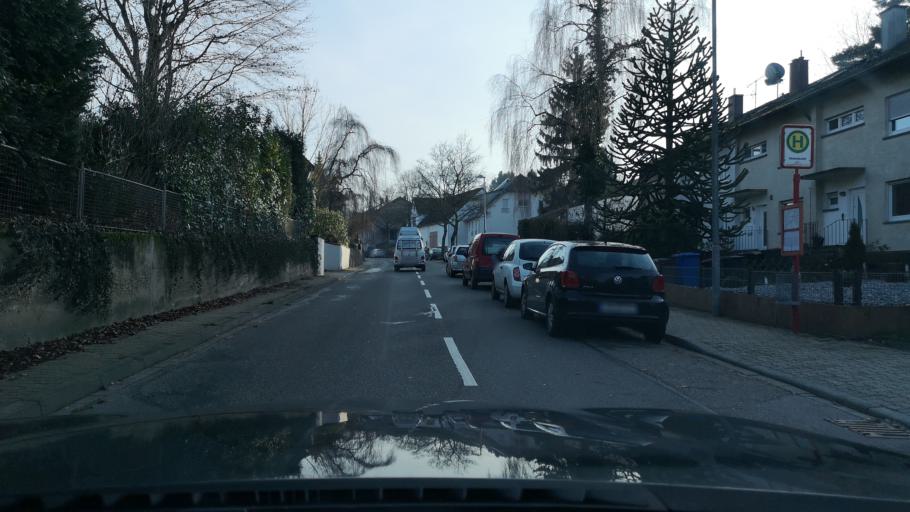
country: DE
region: Baden-Wuerttemberg
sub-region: Karlsruhe Region
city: Ettlingen
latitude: 48.9711
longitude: 8.4761
